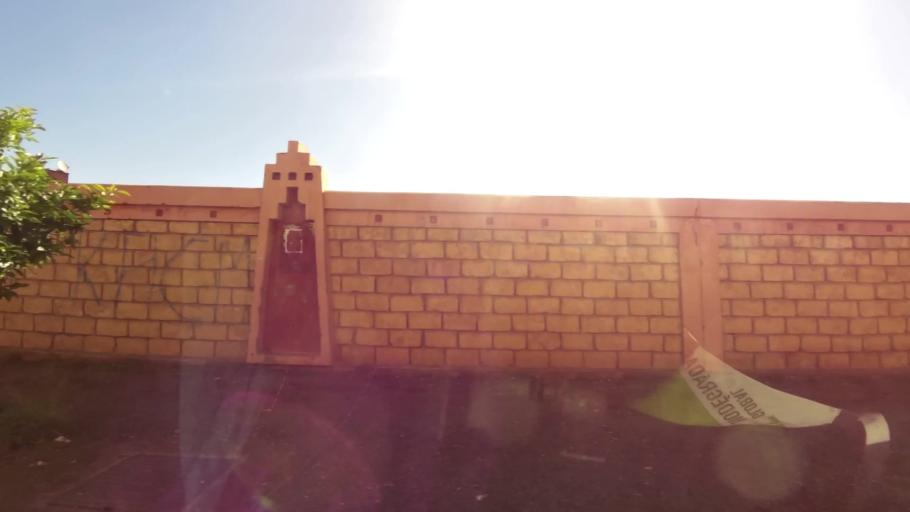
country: MA
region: Marrakech-Tensift-Al Haouz
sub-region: Marrakech
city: Marrakesh
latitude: 31.5923
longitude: -8.0259
